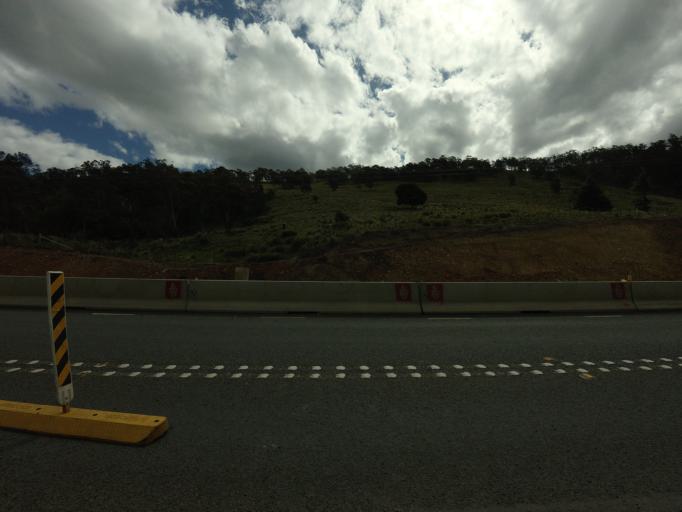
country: AU
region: Tasmania
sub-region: Brighton
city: Bridgewater
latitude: -42.2429
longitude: 147.4044
